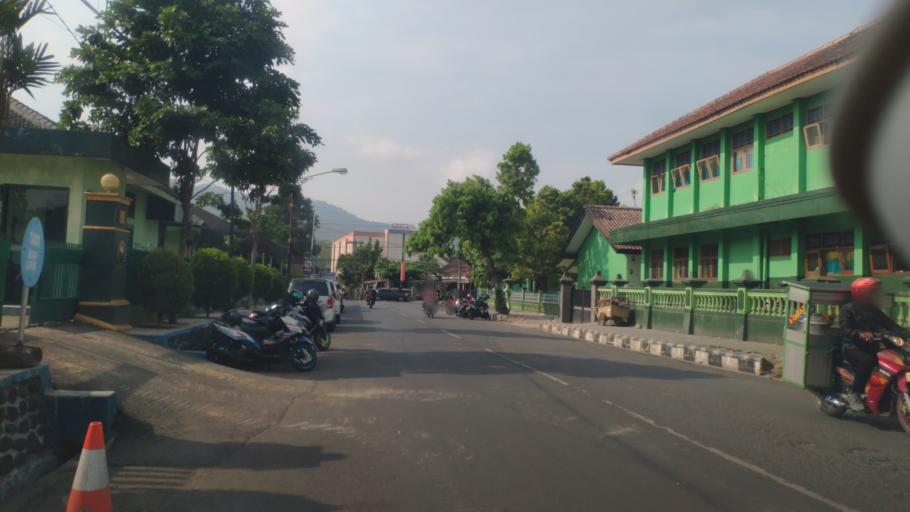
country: ID
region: Central Java
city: Wonosobo
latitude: -7.3972
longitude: 109.6959
